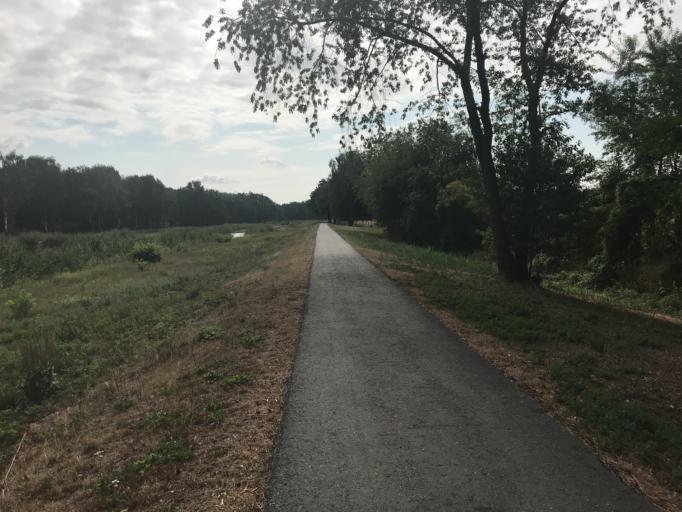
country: DE
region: Brandenburg
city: Schilda
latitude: 51.5835
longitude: 13.3361
